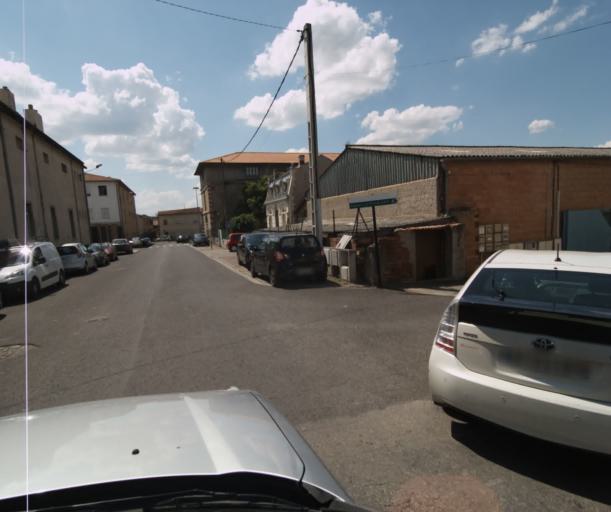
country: FR
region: Languedoc-Roussillon
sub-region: Departement de l'Aude
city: Limoux
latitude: 43.0564
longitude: 2.2218
